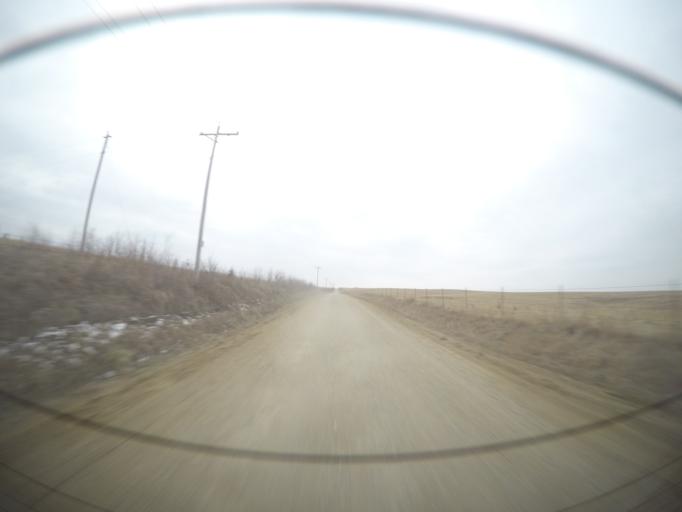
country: US
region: Kansas
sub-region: Pottawatomie County
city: Wamego
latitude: 39.1518
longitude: -96.2512
